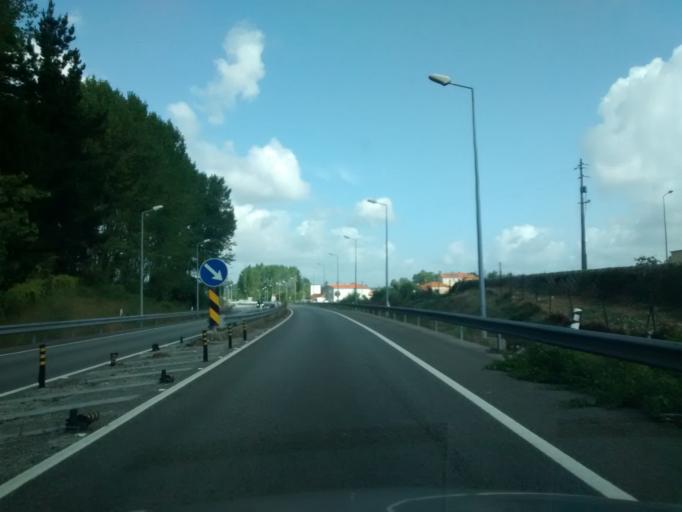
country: PT
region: Aveiro
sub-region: Anadia
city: Sangalhos
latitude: 40.4793
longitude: -8.4771
